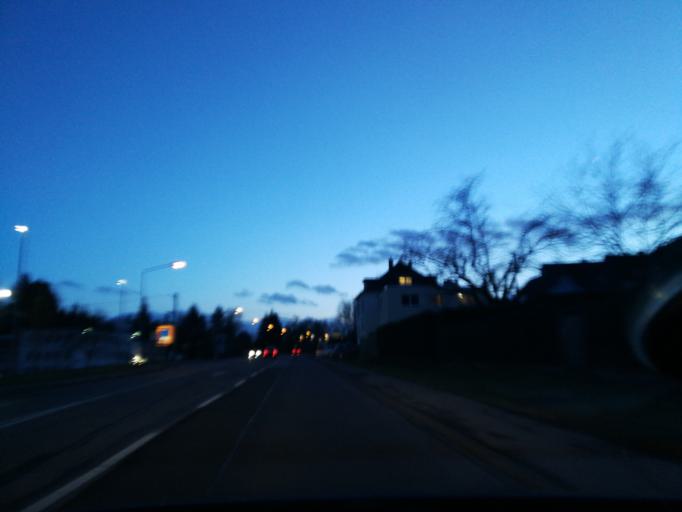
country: DE
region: Rheinland-Pfalz
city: Kenn
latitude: 49.7913
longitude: 6.6788
